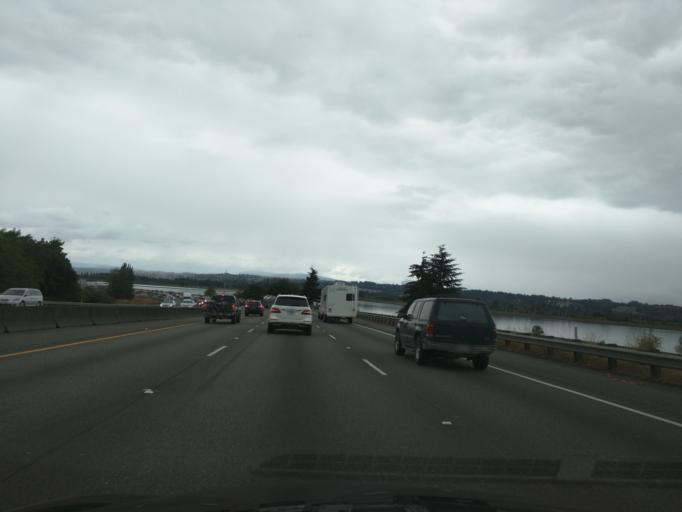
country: US
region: Washington
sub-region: Snohomish County
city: Everett
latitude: 47.9957
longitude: -122.1765
